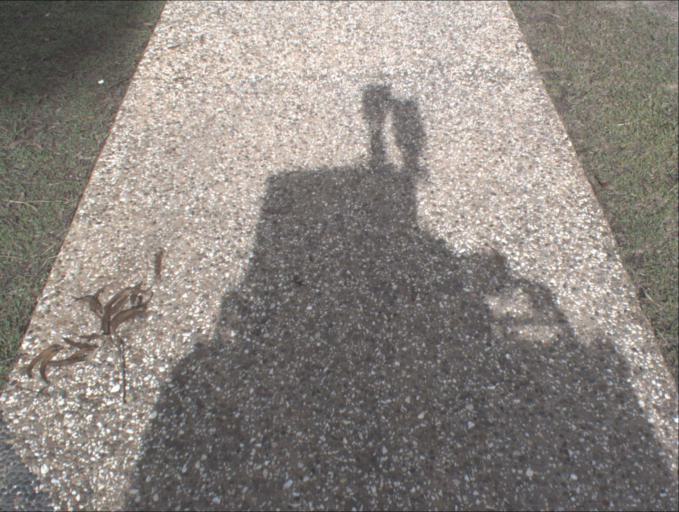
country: AU
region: Queensland
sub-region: Logan
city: Logan Reserve
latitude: -27.6915
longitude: 153.0918
